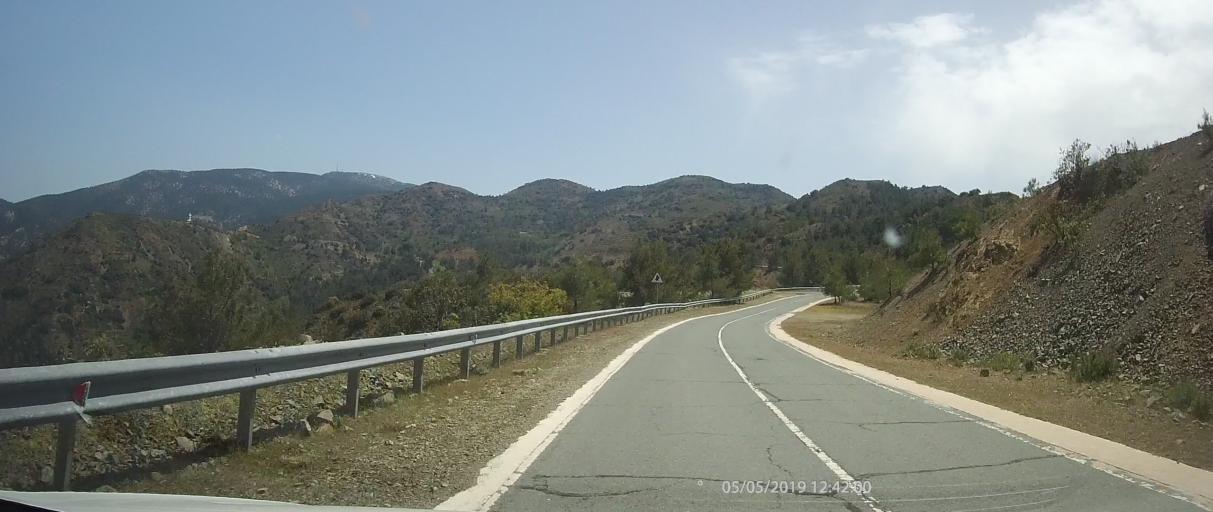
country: CY
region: Lefkosia
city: Kakopetria
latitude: 34.9776
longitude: 32.8097
